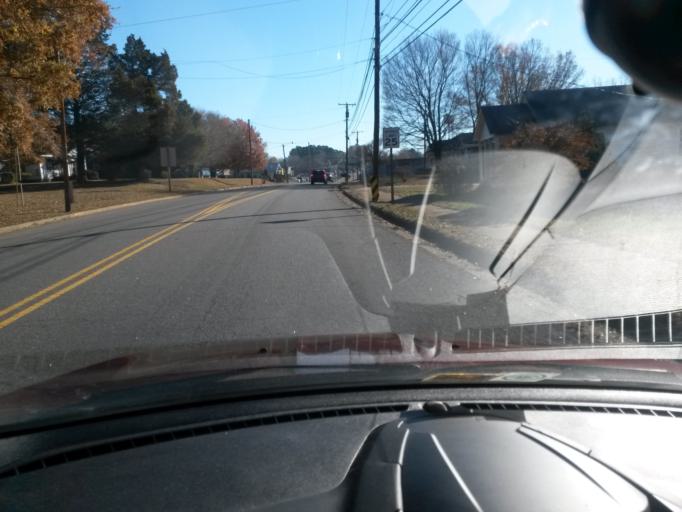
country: US
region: Virginia
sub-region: Charlotte County
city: Charlotte Court House
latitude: 37.0429
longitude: -78.4874
